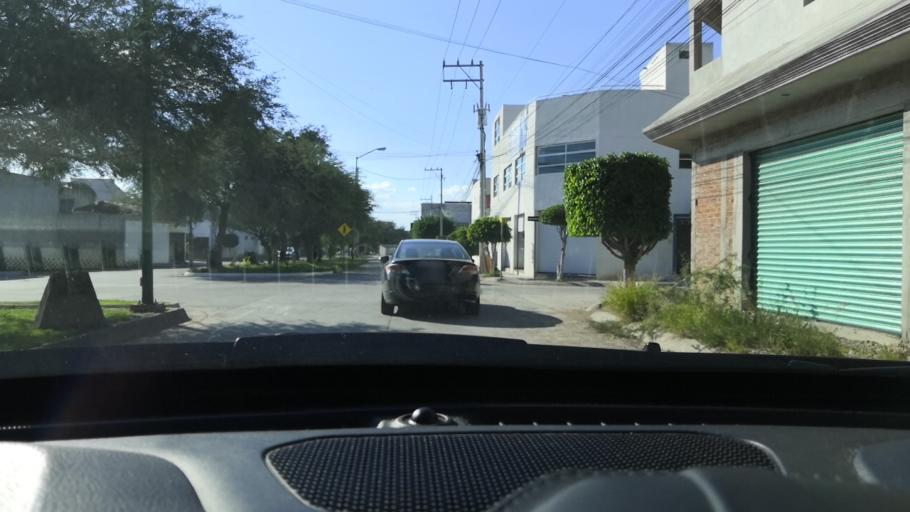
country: MX
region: Guanajuato
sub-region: Leon
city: Medina
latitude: 21.1672
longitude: -101.6437
